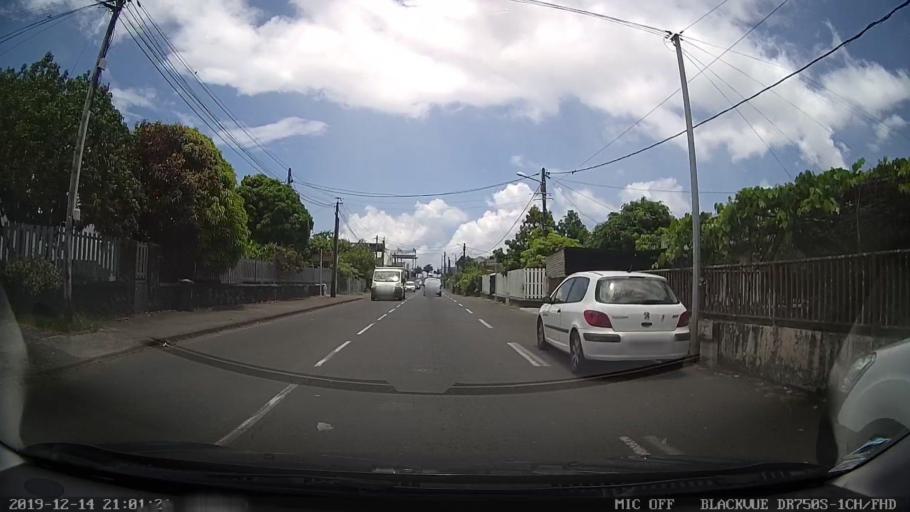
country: RE
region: Reunion
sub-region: Reunion
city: Saint-Andre
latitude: -20.9665
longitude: 55.6595
